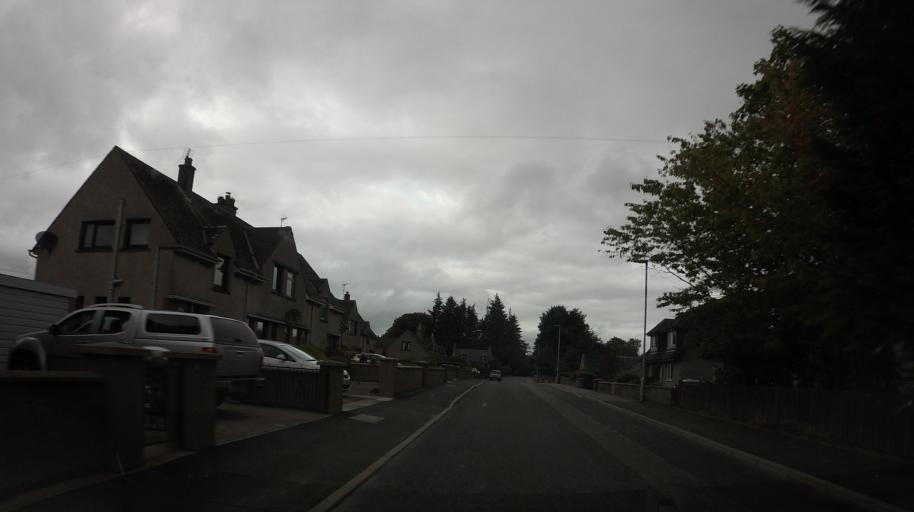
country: GB
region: Scotland
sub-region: Aberdeenshire
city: Alford
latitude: 57.2356
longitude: -2.7032
